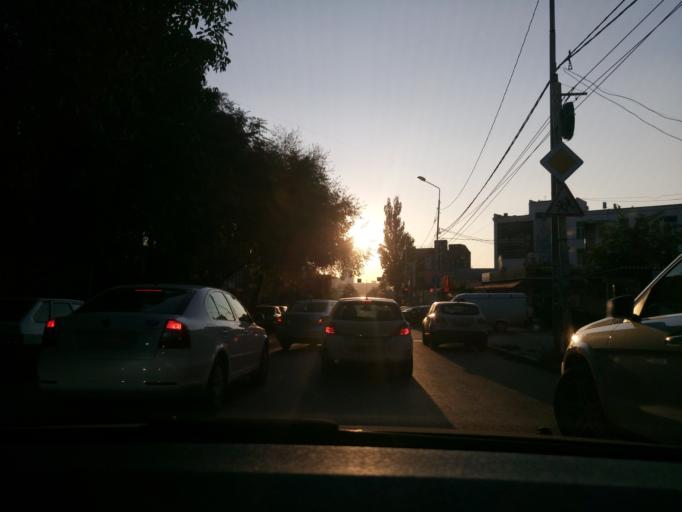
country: RU
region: Rostov
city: Rostov-na-Donu
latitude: 47.2302
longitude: 39.6831
